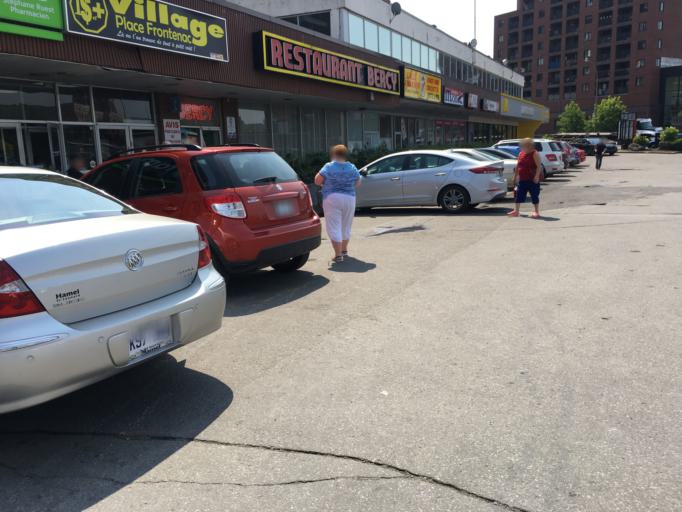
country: CA
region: Quebec
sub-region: Monteregie
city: Longueuil
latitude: 45.5338
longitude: -73.5512
